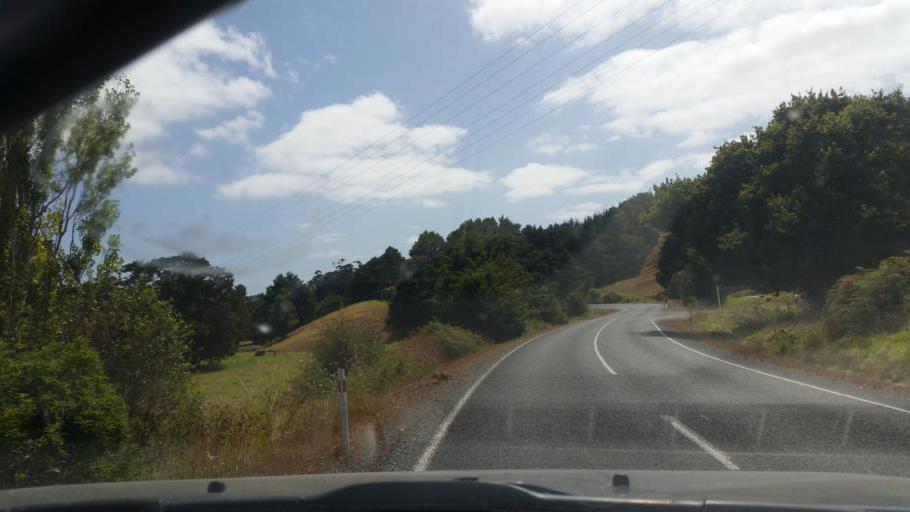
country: NZ
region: Northland
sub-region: Whangarei
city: Ruakaka
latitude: -35.9430
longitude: 174.2916
